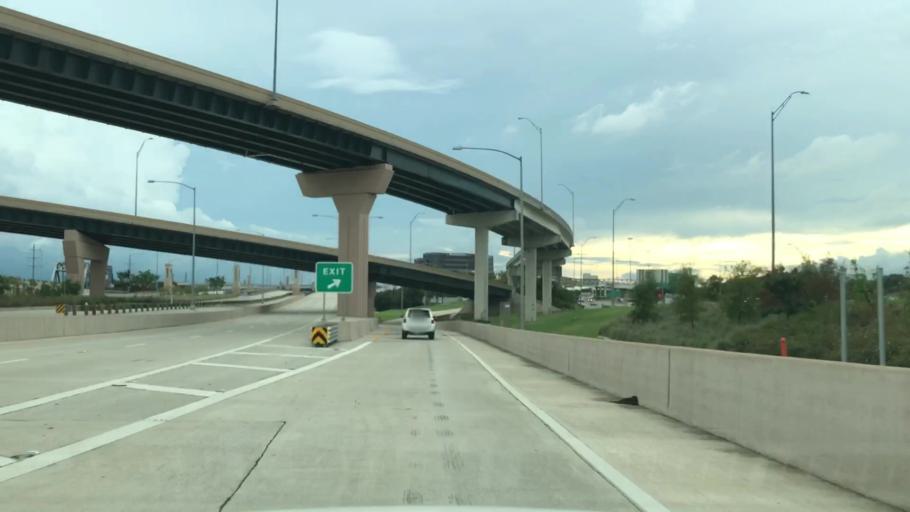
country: US
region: Texas
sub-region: Tarrant County
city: Fort Worth
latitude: 32.7348
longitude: -97.3567
